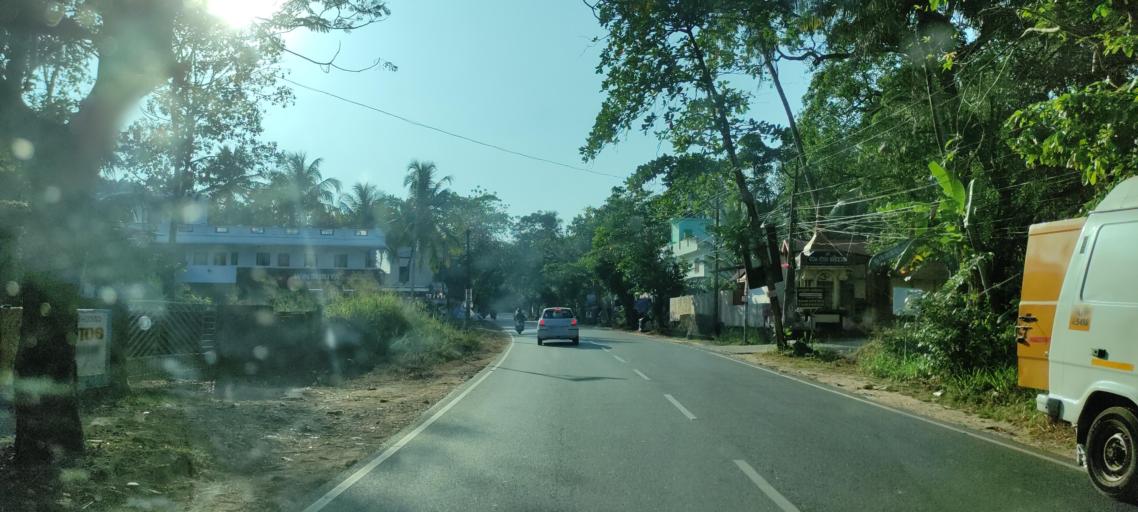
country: IN
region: Kerala
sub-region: Pattanamtitta
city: Adur
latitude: 9.1648
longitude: 76.6919
